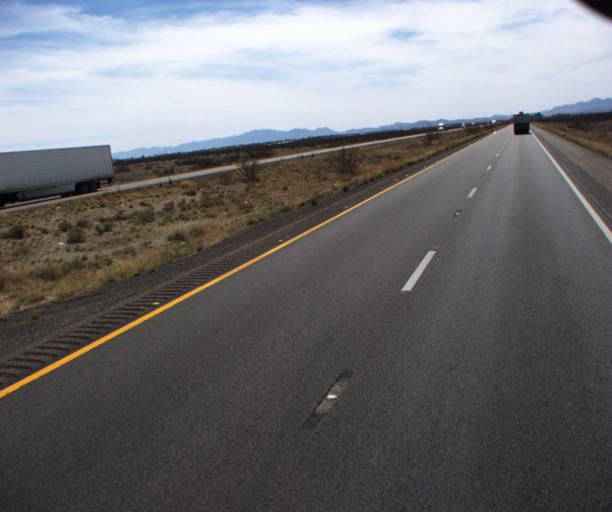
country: US
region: Arizona
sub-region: Cochise County
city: Willcox
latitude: 32.2856
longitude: -109.8244
